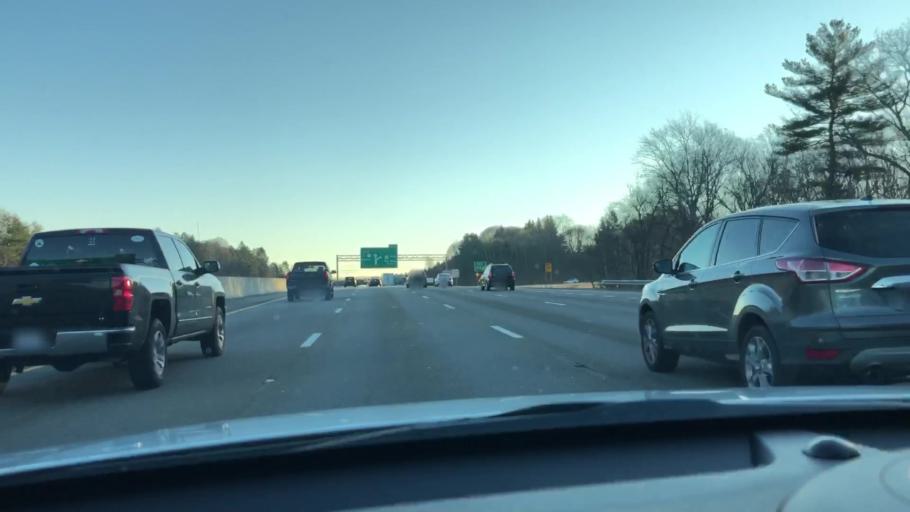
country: US
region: Massachusetts
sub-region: Norfolk County
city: Canton
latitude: 42.2039
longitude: -71.1247
